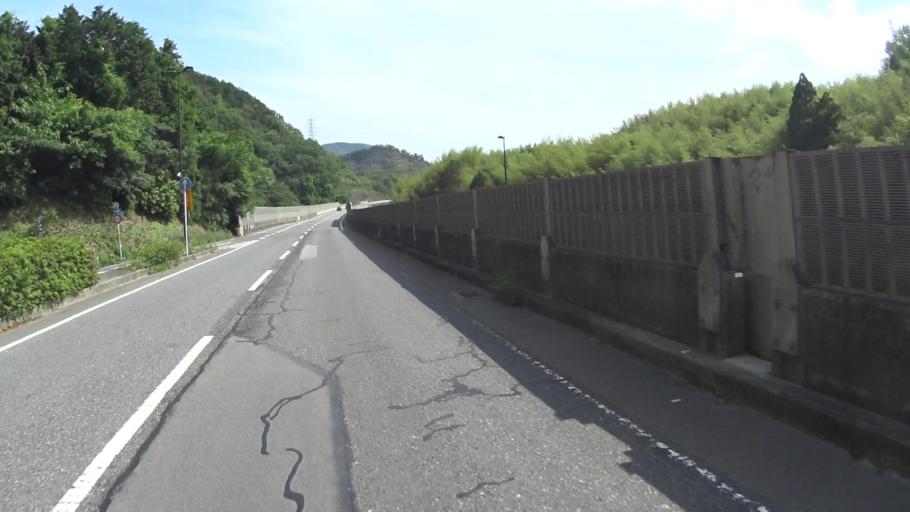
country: JP
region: Shiga Prefecture
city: Otsu-shi
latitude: 35.0040
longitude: 135.8376
